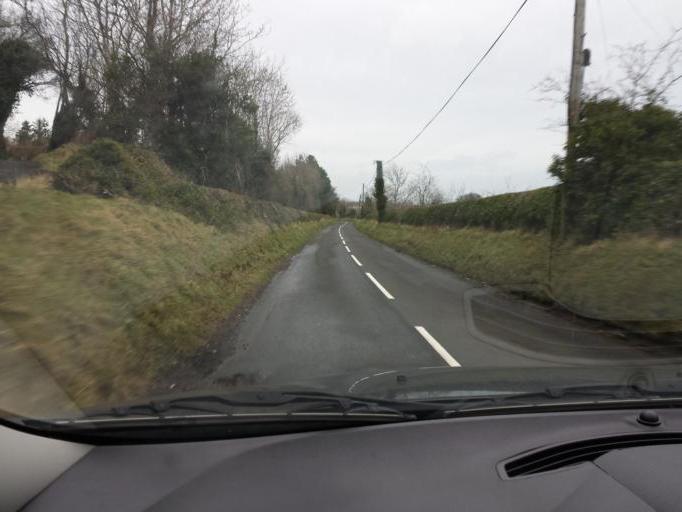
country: GB
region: Northern Ireland
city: Cushendall
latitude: 55.0758
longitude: -6.0991
